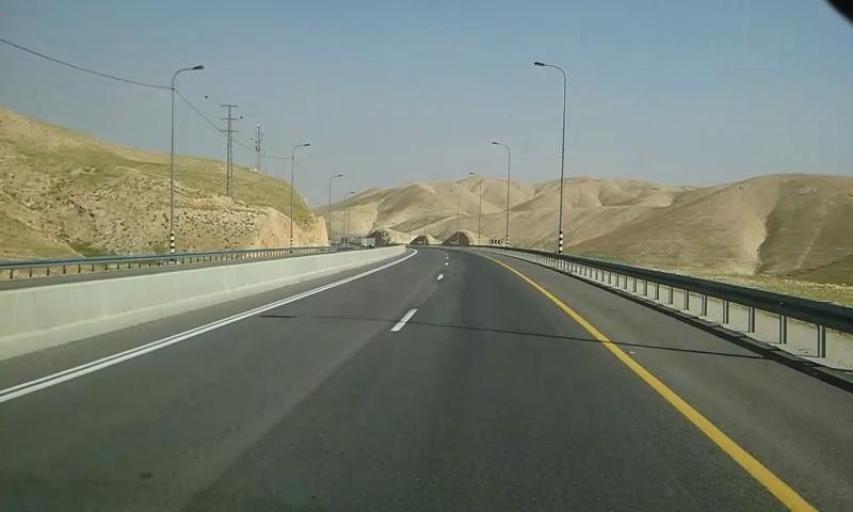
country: PS
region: West Bank
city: Jericho
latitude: 31.8157
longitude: 35.3682
